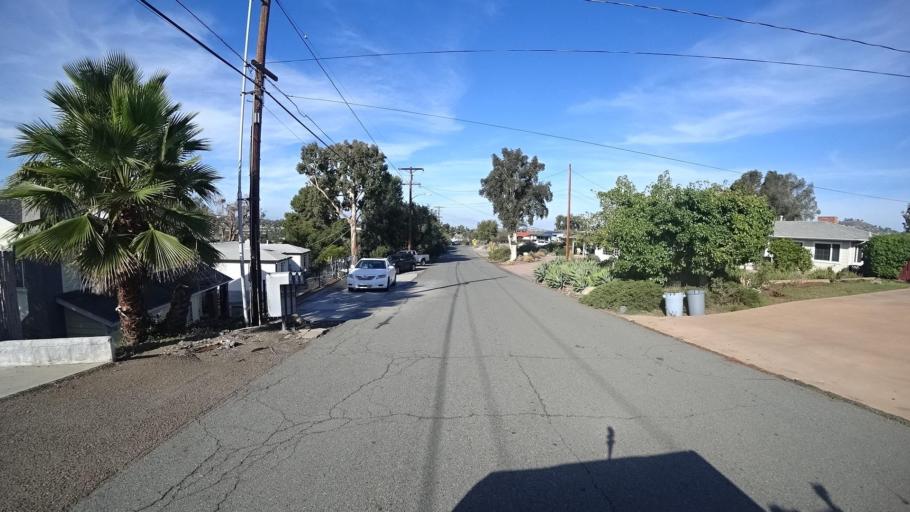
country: US
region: California
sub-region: San Diego County
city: Casa de Oro-Mount Helix
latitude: 32.7377
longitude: -116.9683
